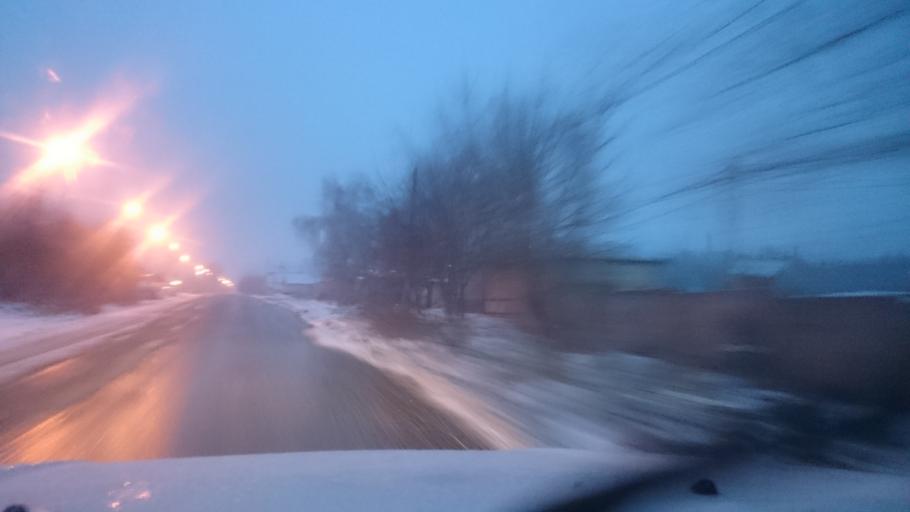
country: RU
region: Tula
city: Barsuki
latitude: 54.2037
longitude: 37.5358
